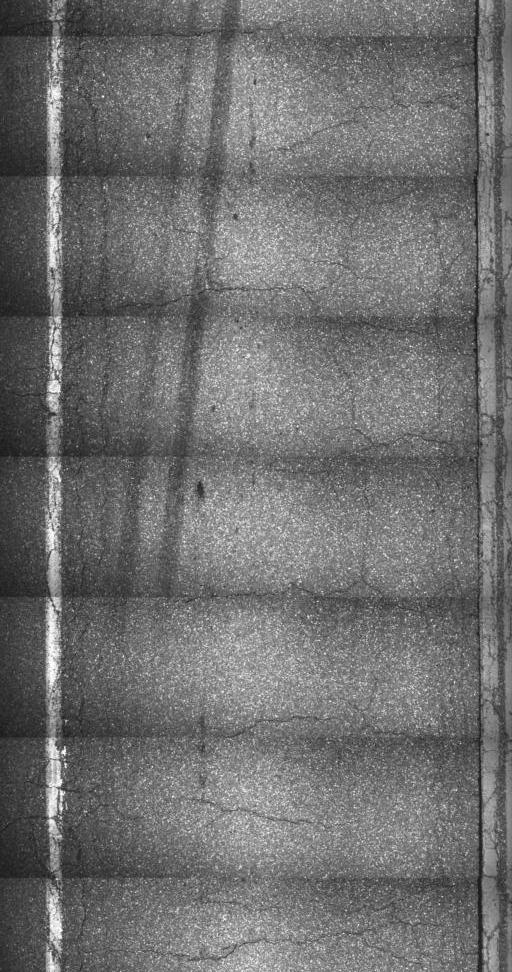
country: US
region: Vermont
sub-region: Lamoille County
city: Morrisville
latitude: 44.5680
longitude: -72.5811
